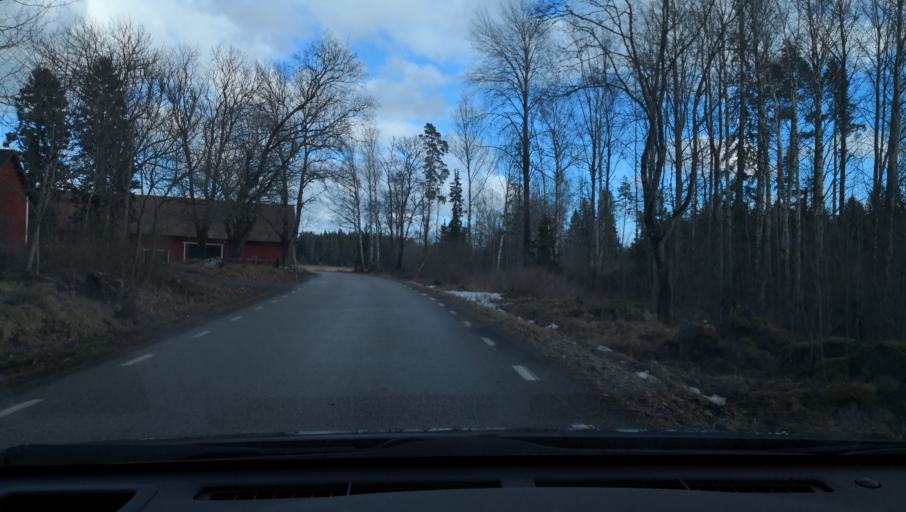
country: SE
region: OErebro
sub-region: Lindesbergs Kommun
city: Fellingsbro
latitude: 59.3391
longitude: 15.6945
